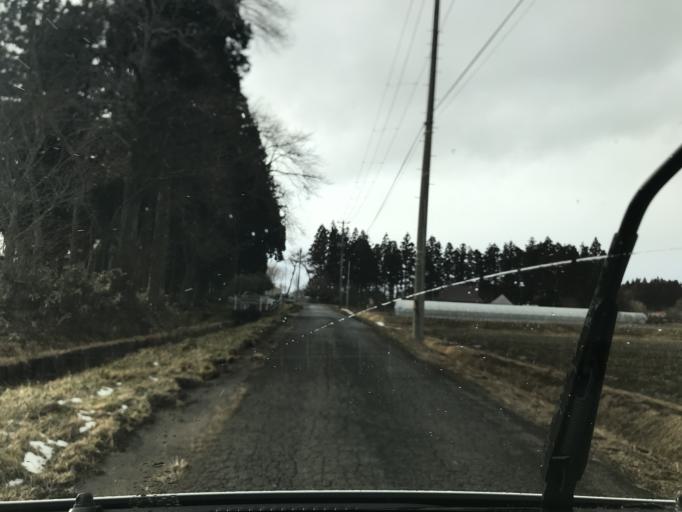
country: JP
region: Iwate
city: Mizusawa
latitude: 39.0843
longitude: 141.0383
